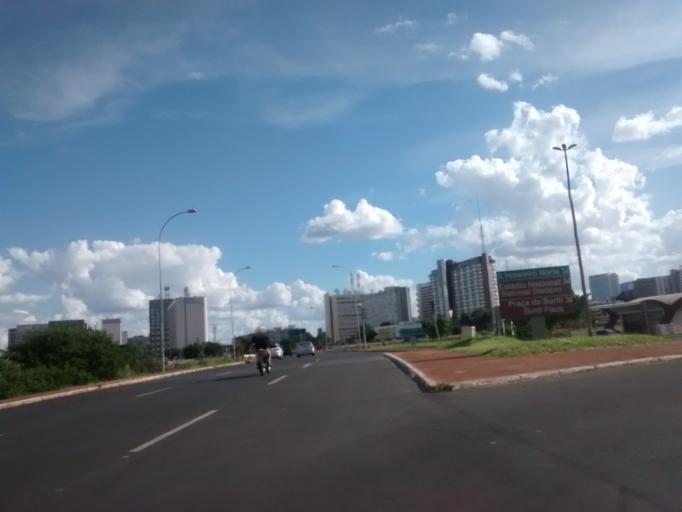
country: BR
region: Federal District
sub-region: Brasilia
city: Brasilia
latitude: -15.7910
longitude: -47.8846
